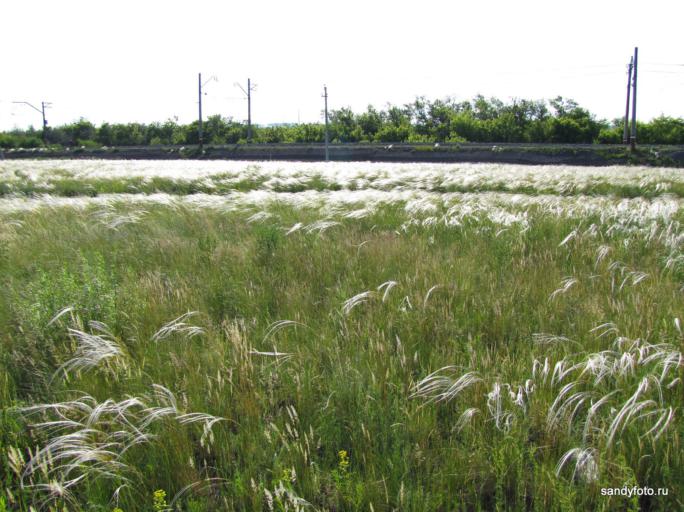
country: RU
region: Chelyabinsk
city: Troitsk
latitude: 54.0689
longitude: 61.6252
